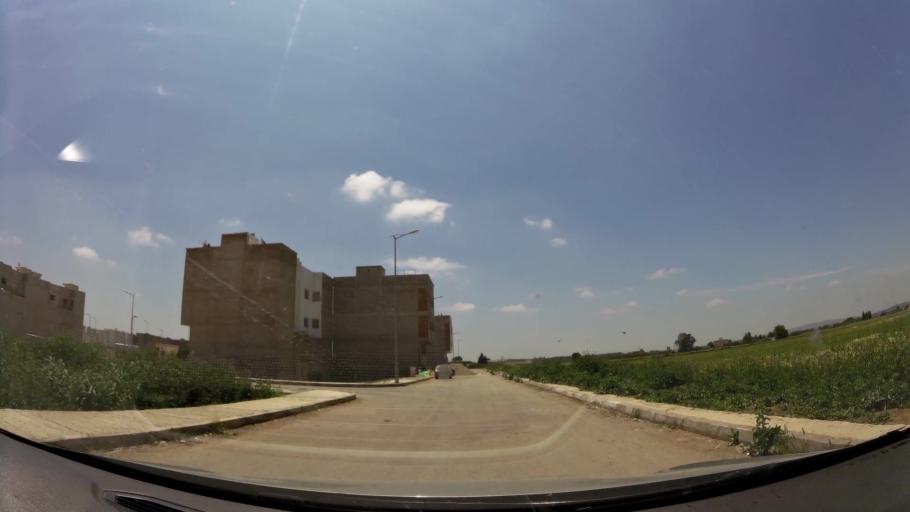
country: MA
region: Fes-Boulemane
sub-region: Fes
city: Fes
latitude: 34.0236
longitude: -5.0604
